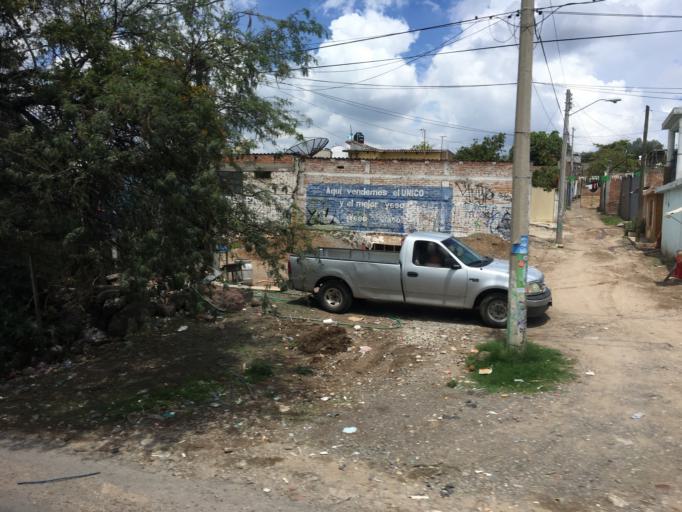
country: MX
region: Guanajuato
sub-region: Irapuato
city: Ex-Hacienda del Copal
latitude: 20.7293
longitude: -101.3435
